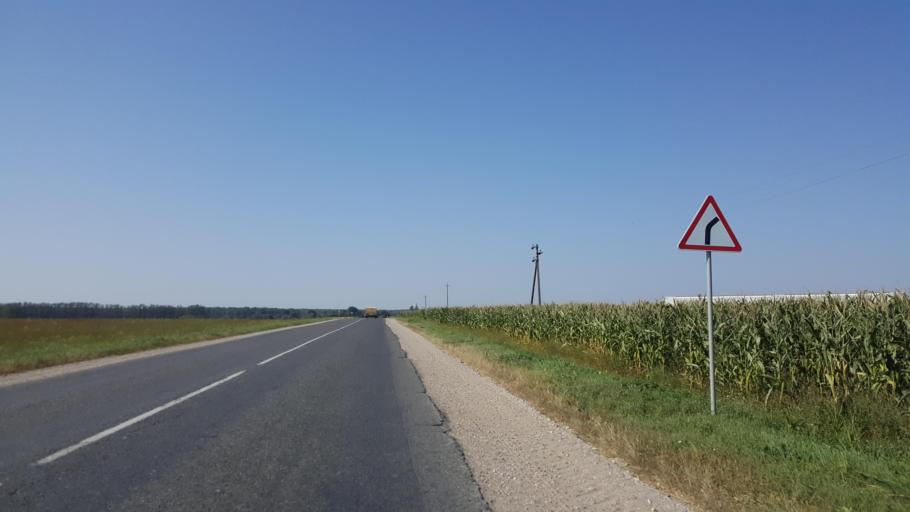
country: BY
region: Brest
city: Kamyanyets
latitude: 52.4147
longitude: 23.6093
